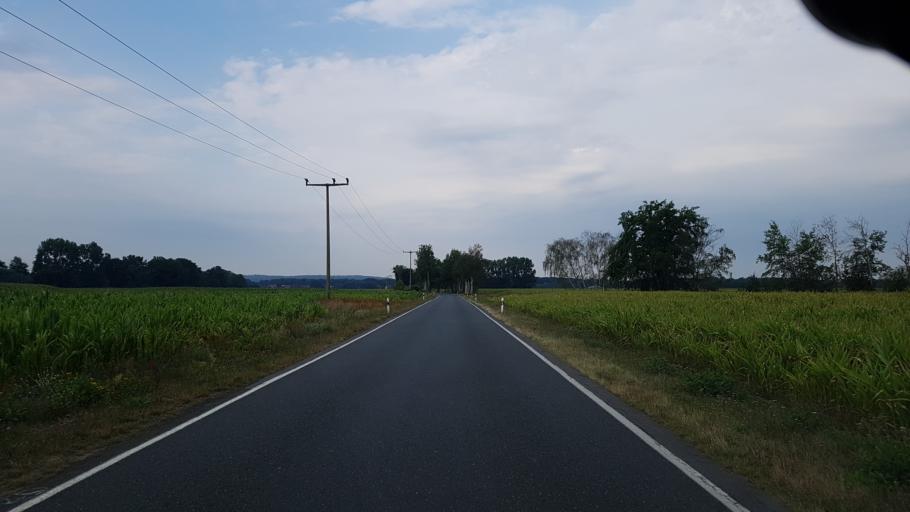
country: DE
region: Brandenburg
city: Lindenau
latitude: 51.4150
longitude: 13.7252
